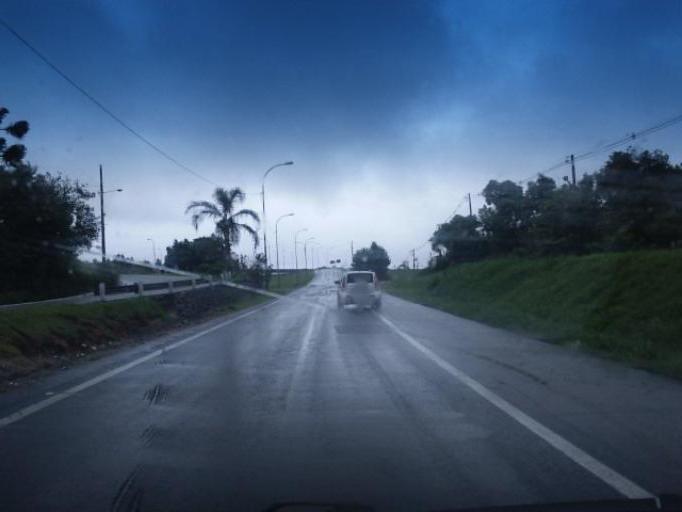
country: BR
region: Parana
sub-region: Sao Jose Dos Pinhais
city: Sao Jose dos Pinhais
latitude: -25.5713
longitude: -49.1801
